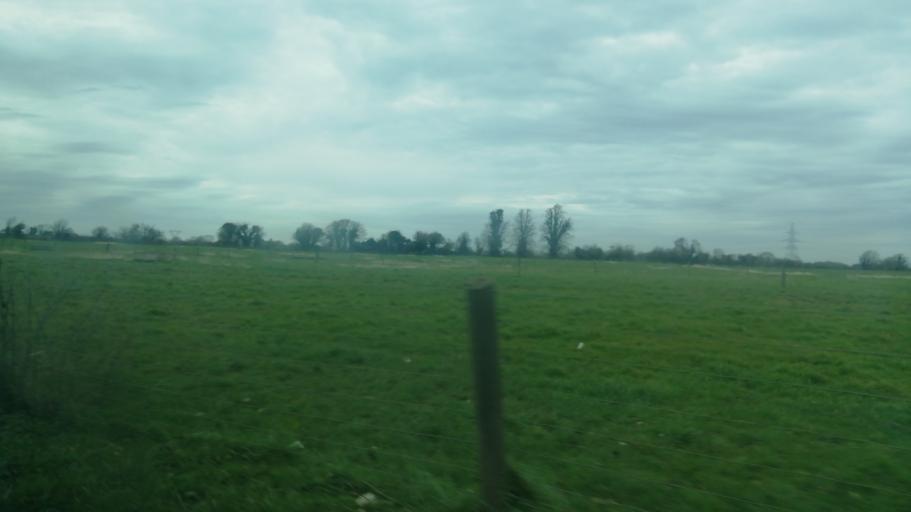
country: IE
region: Leinster
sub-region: Kildare
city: Maynooth
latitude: 53.3528
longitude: -6.6115
